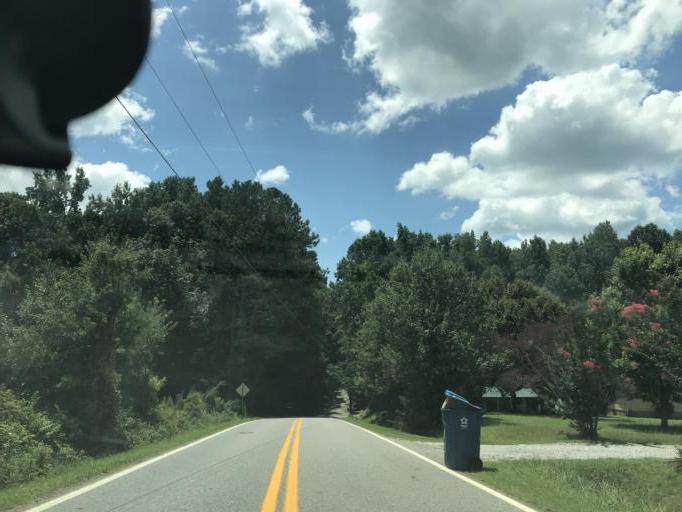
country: US
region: Georgia
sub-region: Fulton County
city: Milton
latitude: 34.2142
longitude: -84.2579
